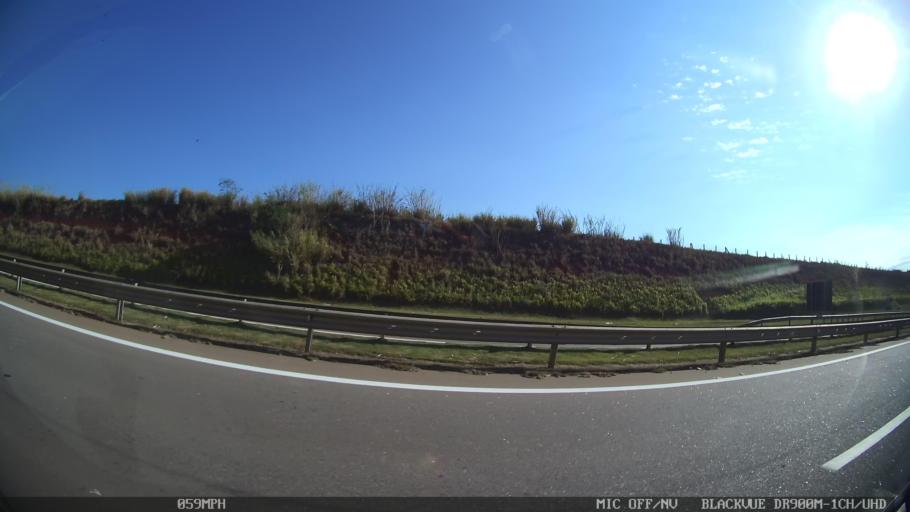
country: BR
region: Sao Paulo
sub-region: Piracicaba
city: Piracicaba
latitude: -22.7106
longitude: -47.6103
